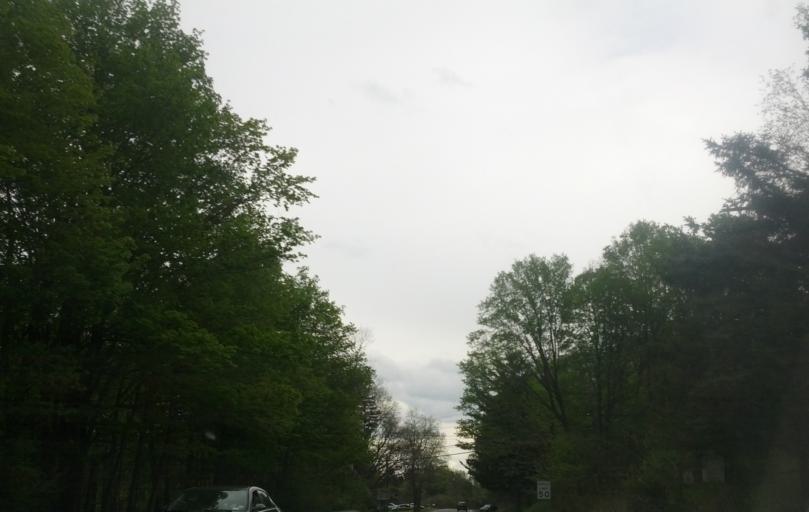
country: US
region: New York
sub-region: Onondaga County
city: Nedrow
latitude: 42.9962
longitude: -76.1080
